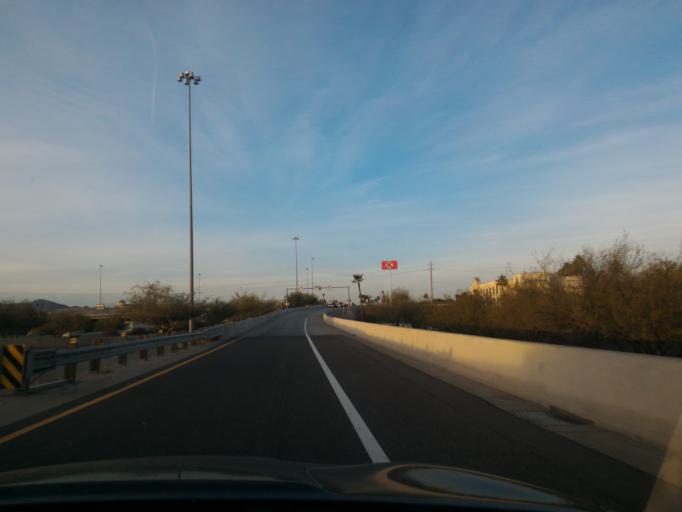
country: US
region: Arizona
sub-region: Maricopa County
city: Guadalupe
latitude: 33.3029
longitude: -111.9712
